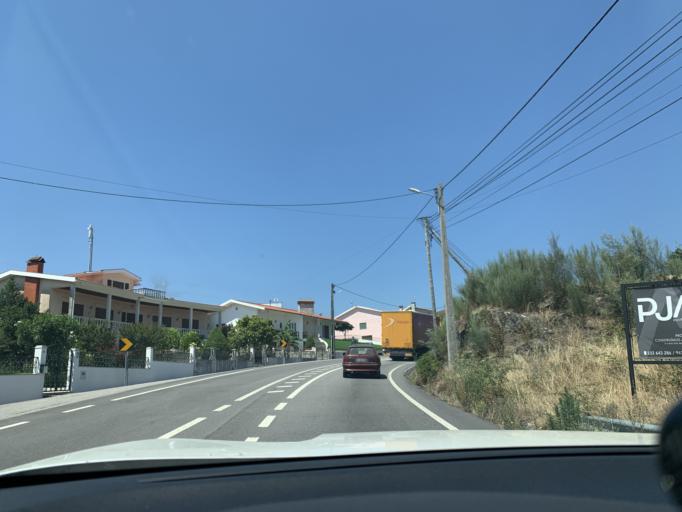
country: PT
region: Viseu
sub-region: Mangualde
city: Mangualde
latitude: 40.5993
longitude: -7.7918
